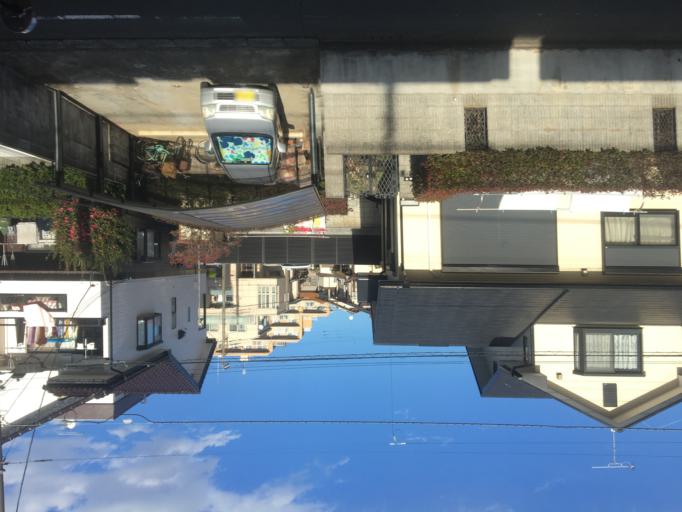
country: JP
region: Saitama
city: Oi
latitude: 35.8407
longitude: 139.5472
